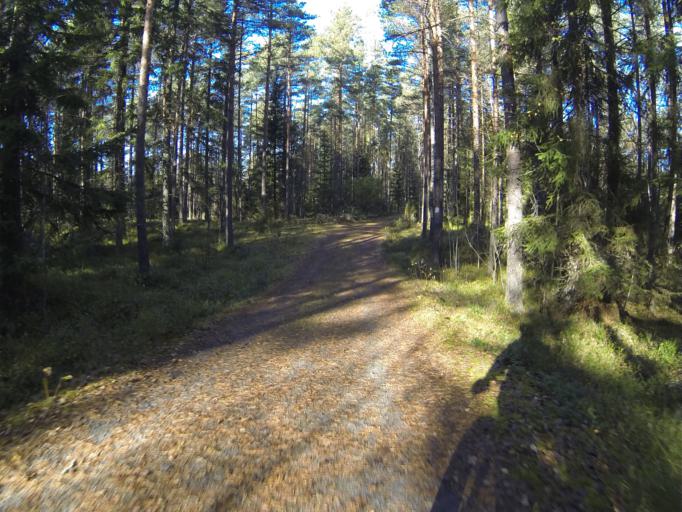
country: FI
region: Varsinais-Suomi
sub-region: Salo
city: Saerkisalo
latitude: 60.2099
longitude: 22.9253
